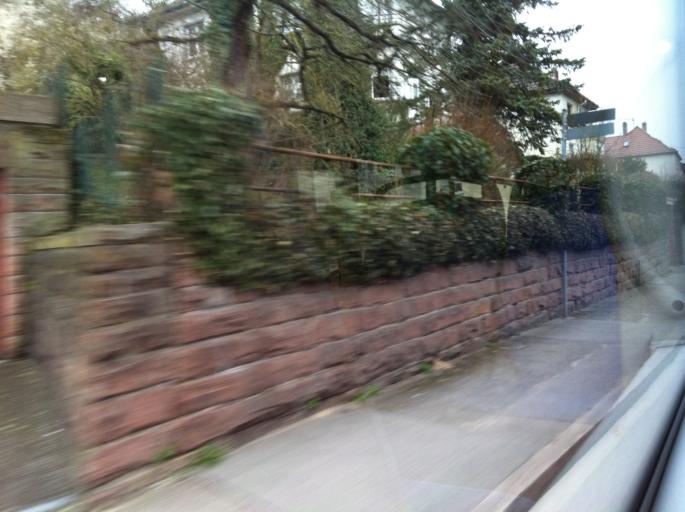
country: DE
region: Baden-Wuerttemberg
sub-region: Karlsruhe Region
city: Mosbach
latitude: 49.3500
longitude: 9.1321
